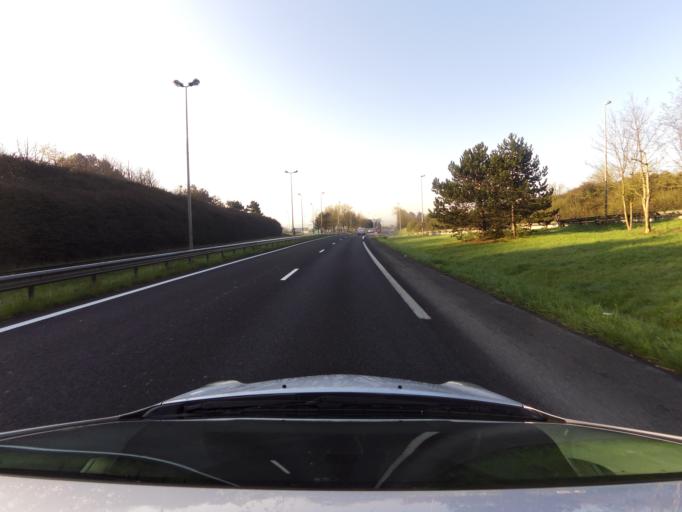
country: FR
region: Lower Normandy
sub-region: Departement du Calvados
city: Authie
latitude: 49.1897
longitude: -0.4240
